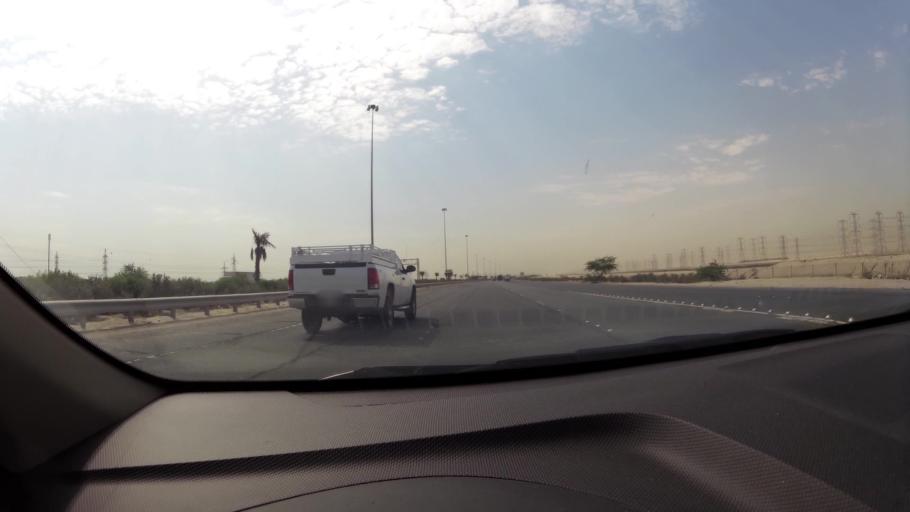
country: KW
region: Al Ahmadi
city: Al Fahahil
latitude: 28.9106
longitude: 48.2130
